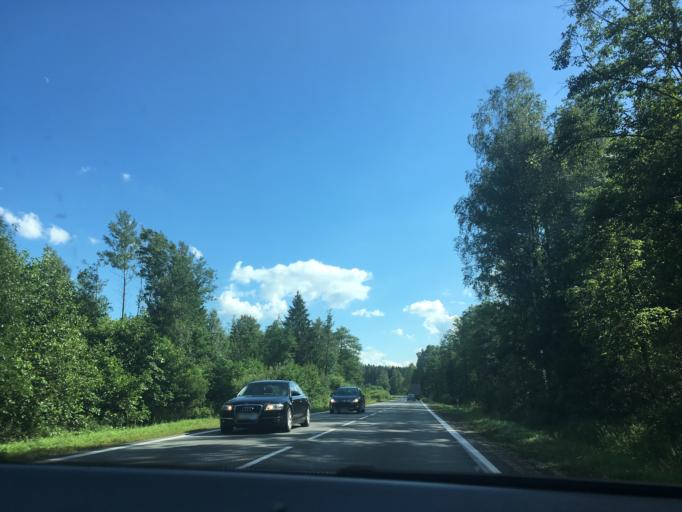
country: PL
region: Podlasie
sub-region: Powiat bialostocki
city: Wasilkow
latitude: 53.2767
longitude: 23.1204
